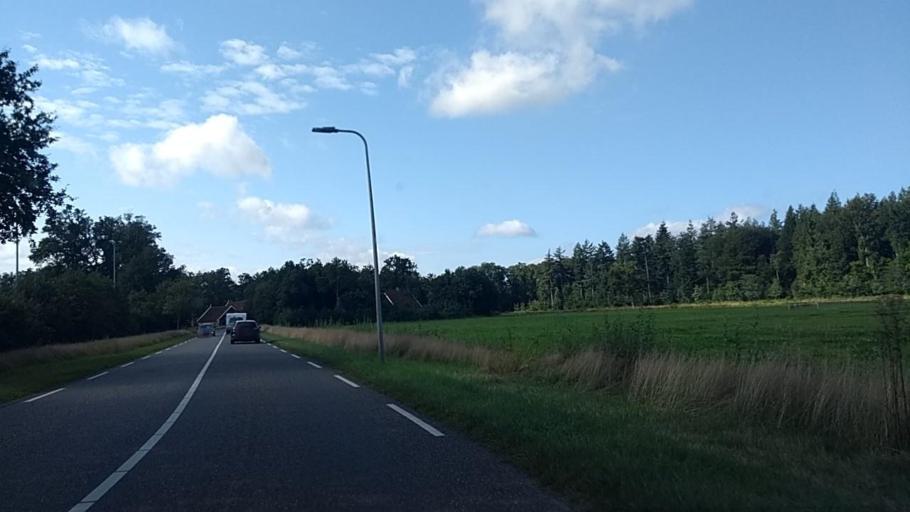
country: NL
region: Overijssel
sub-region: Gemeente Oldenzaal
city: Oldenzaal
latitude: 52.3768
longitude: 6.9940
